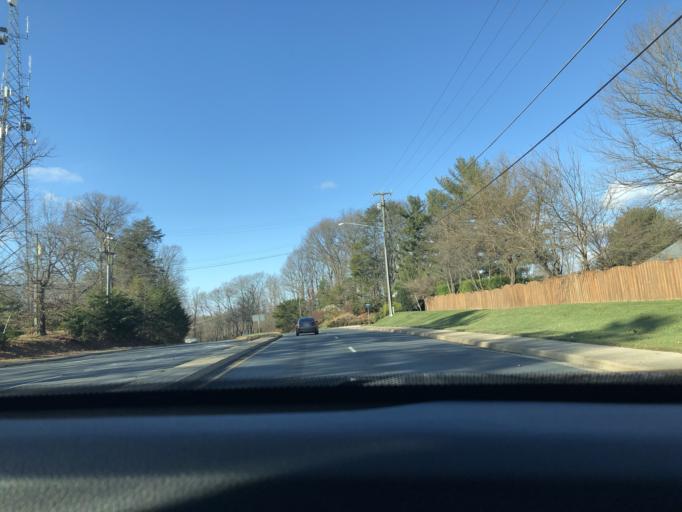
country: US
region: Virginia
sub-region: City of Fairfax
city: Fairfax
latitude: 38.8245
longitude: -77.2824
